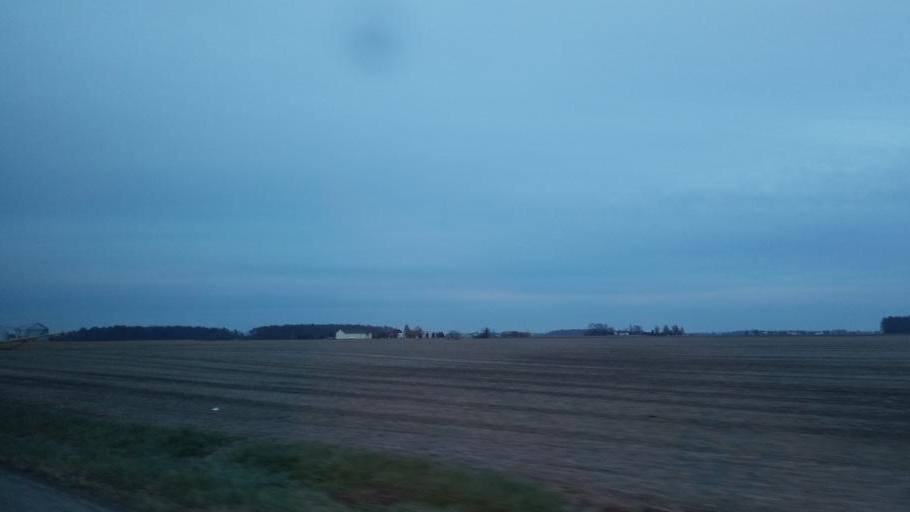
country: US
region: Indiana
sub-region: Adams County
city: Decatur
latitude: 40.7677
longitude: -85.0141
